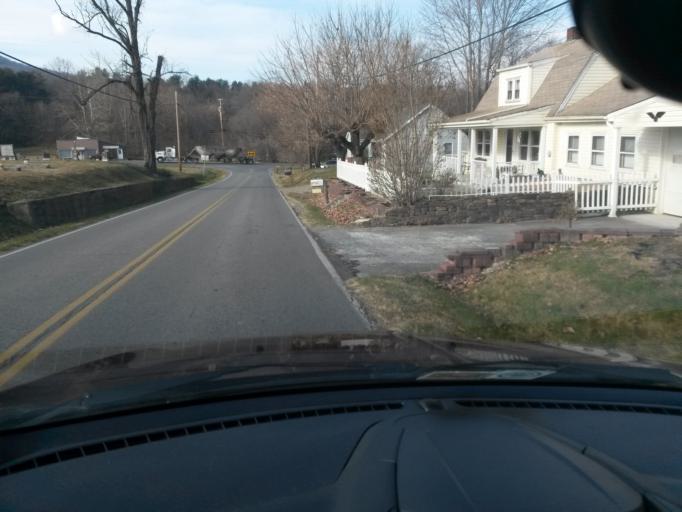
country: US
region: Virginia
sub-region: Botetourt County
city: Daleville
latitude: 37.4517
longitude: -79.9696
